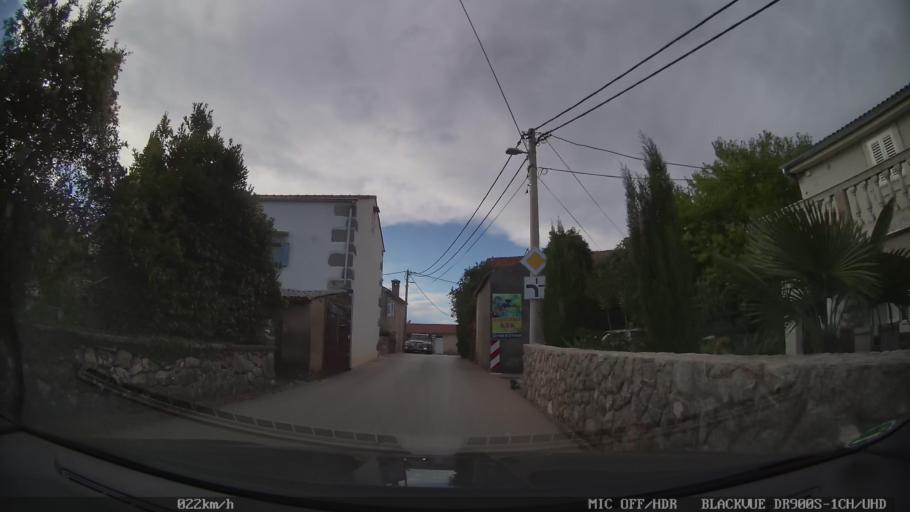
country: HR
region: Primorsko-Goranska
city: Njivice
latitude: 45.0801
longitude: 14.4576
